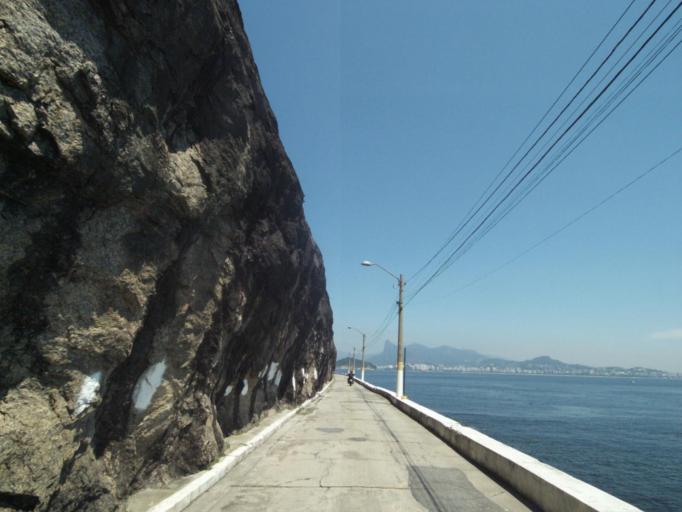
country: BR
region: Rio de Janeiro
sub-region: Niteroi
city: Niteroi
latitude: -22.9311
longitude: -43.1249
